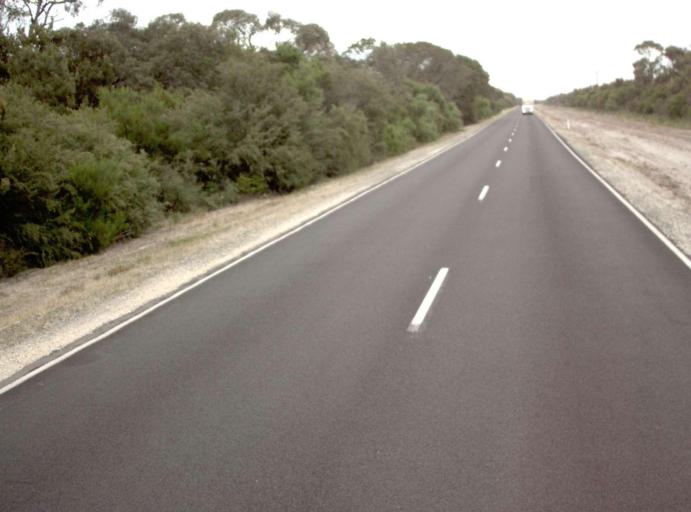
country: AU
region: Victoria
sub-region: East Gippsland
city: Bairnsdale
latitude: -38.0951
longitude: 147.5132
